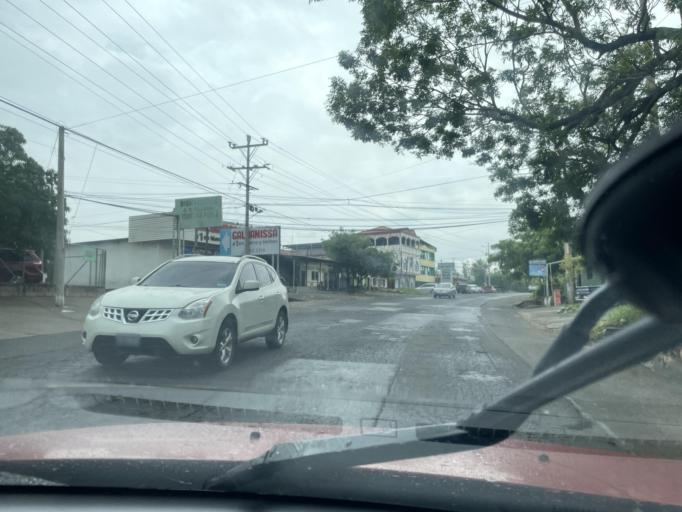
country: SV
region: La Union
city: Santa Rosa de Lima
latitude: 13.6183
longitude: -87.9014
